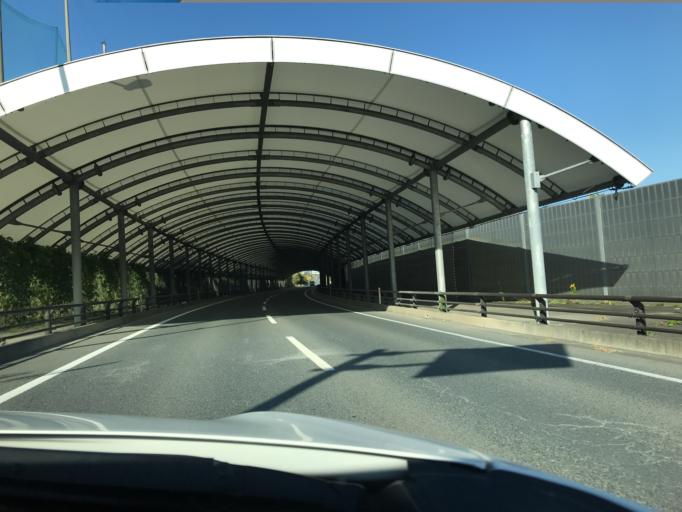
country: JP
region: Miyagi
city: Marumori
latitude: 37.7797
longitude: 140.9402
